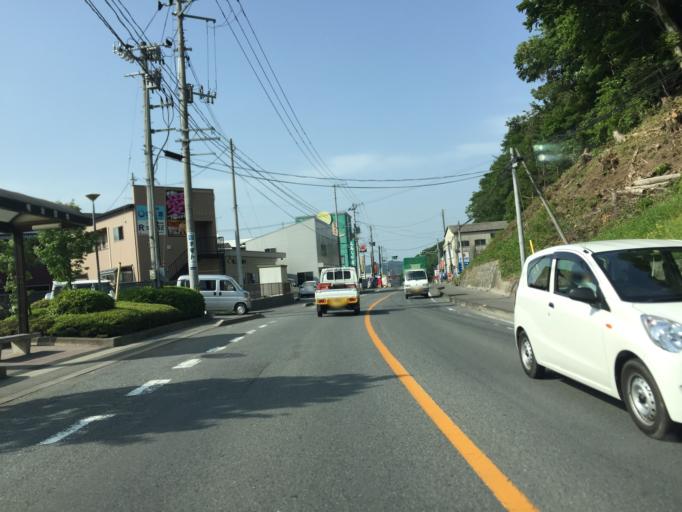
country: JP
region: Fukushima
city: Iwaki
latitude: 37.0402
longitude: 140.8920
